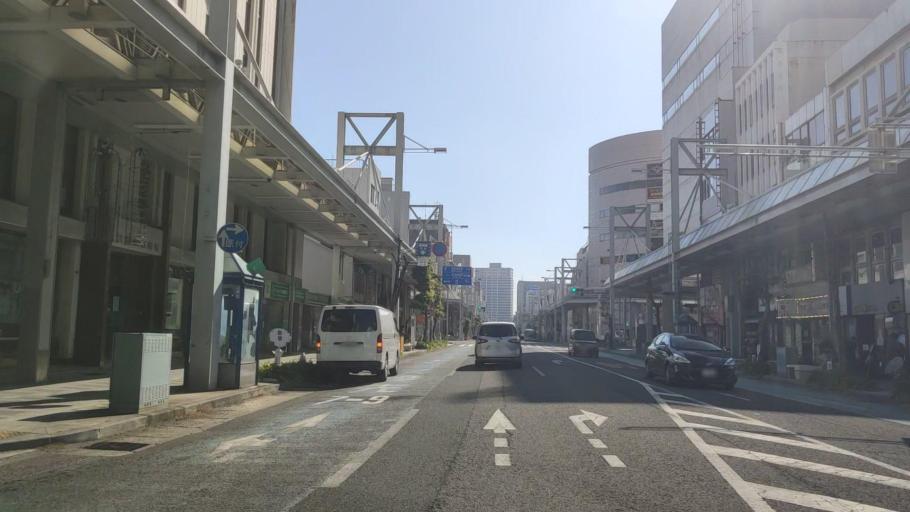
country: JP
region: Gifu
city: Gifu-shi
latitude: 35.4180
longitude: 136.7601
